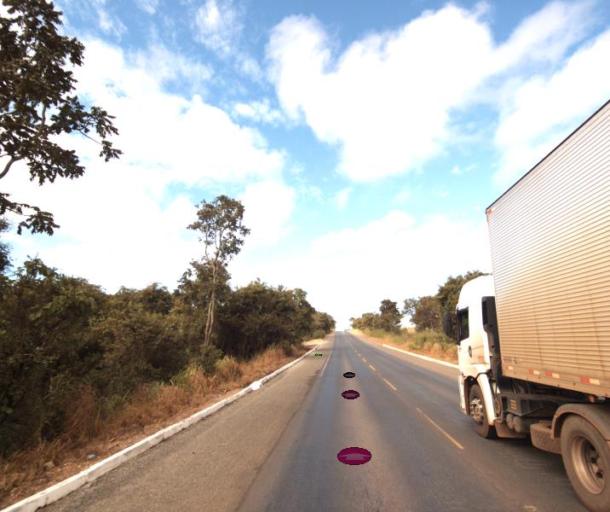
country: BR
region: Goias
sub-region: Uruacu
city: Uruacu
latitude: -14.7873
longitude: -49.2766
